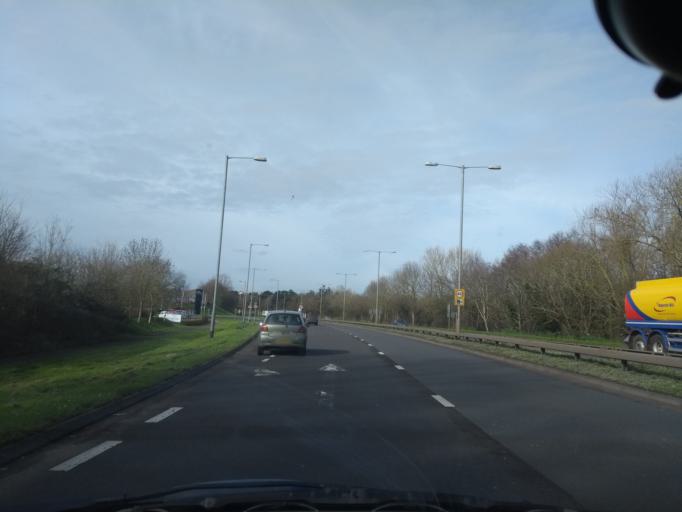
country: GB
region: England
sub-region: Somerset
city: Taunton
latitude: 51.0249
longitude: -3.0783
